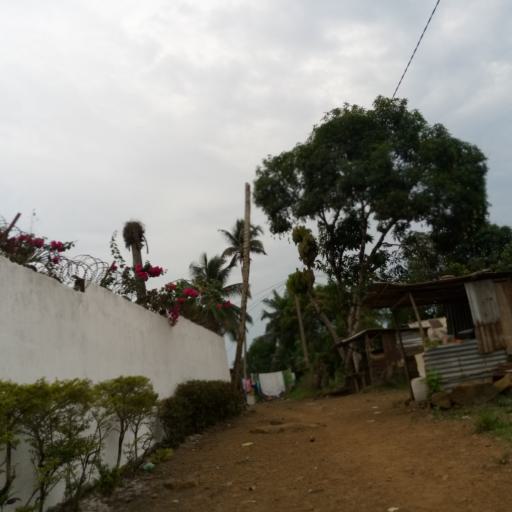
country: LR
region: Montserrado
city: Monrovia
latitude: 6.2927
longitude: -10.6776
